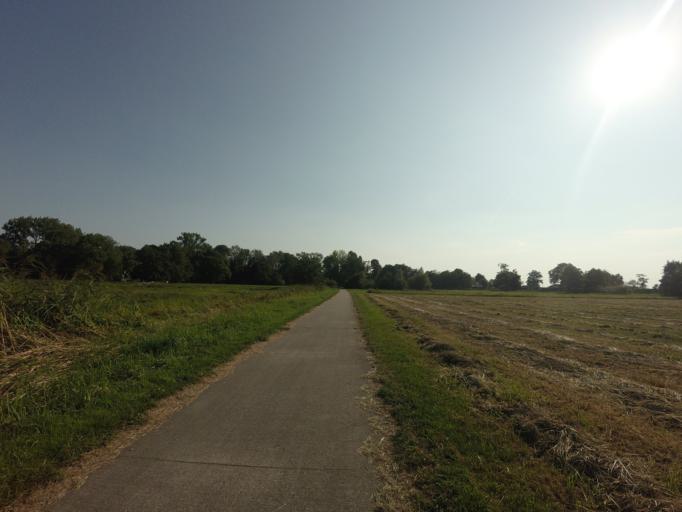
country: NL
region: Groningen
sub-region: Gemeente Zuidhorn
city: Aduard
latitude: 53.1963
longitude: 6.4505
